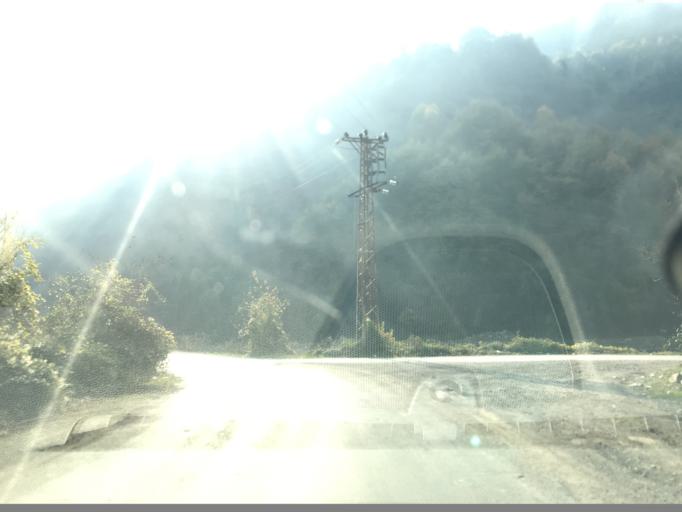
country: TR
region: Duzce
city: Cumayeri
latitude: 40.9296
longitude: 30.9256
